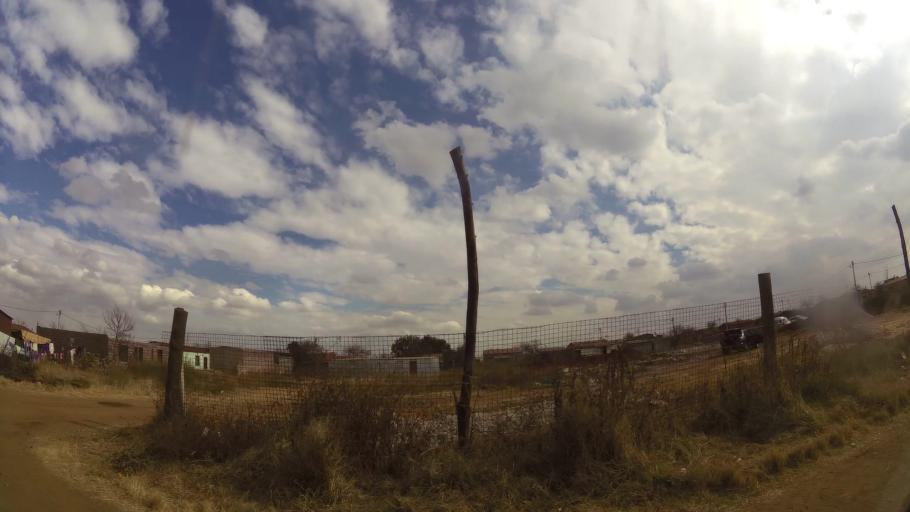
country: ZA
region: Gauteng
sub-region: Ekurhuleni Metropolitan Municipality
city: Germiston
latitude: -26.4104
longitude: 28.1571
